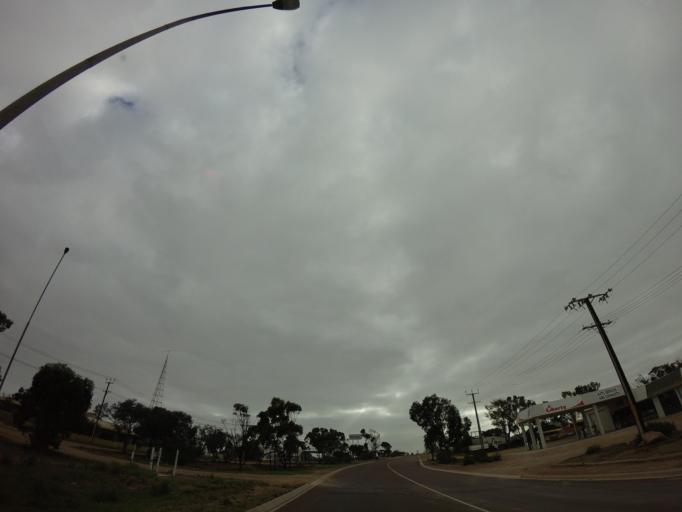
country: AU
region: South Australia
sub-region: Ceduna
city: Ceduna
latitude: -32.1222
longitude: 133.6852
